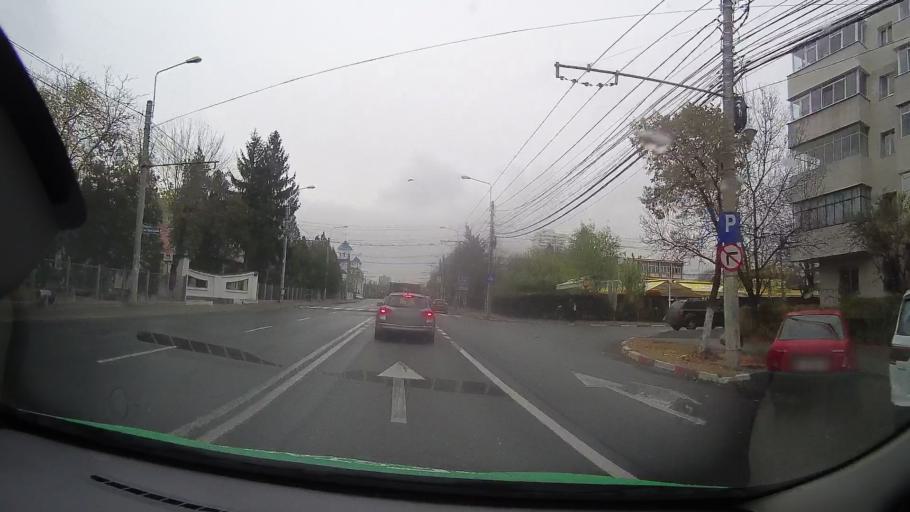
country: RO
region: Prahova
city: Ploiesti
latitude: 44.9381
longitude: 25.9930
